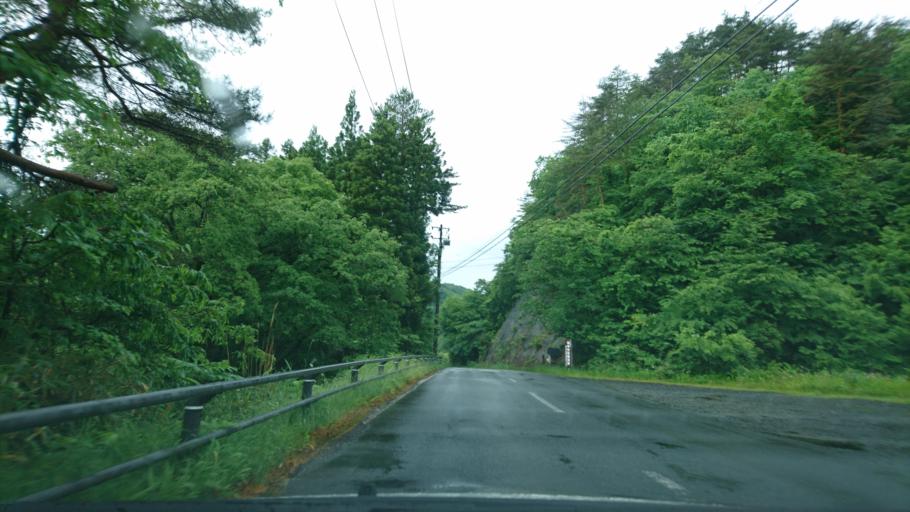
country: JP
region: Iwate
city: Ichinoseki
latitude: 38.9734
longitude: 140.9828
